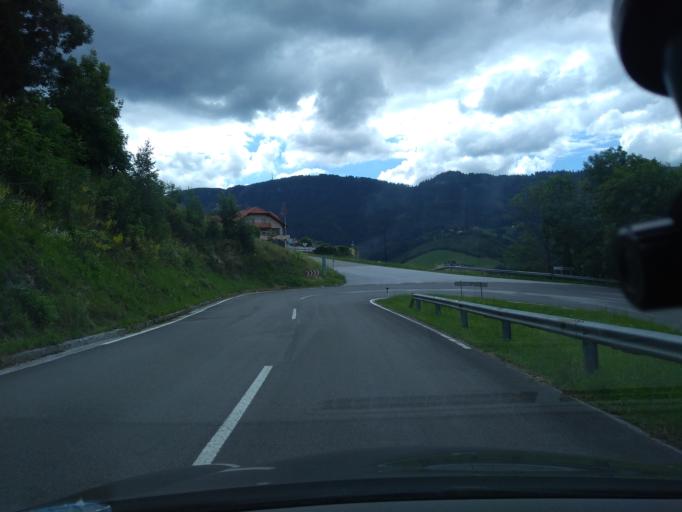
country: AT
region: Styria
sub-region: Politischer Bezirk Graz-Umgebung
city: Semriach
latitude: 47.2206
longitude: 15.4264
